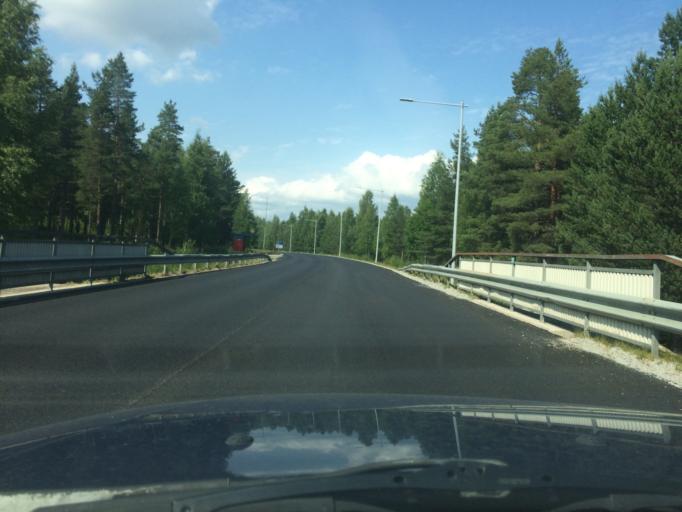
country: SE
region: Norrbotten
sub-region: Pitea Kommun
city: Pitea
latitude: 65.3286
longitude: 21.4726
